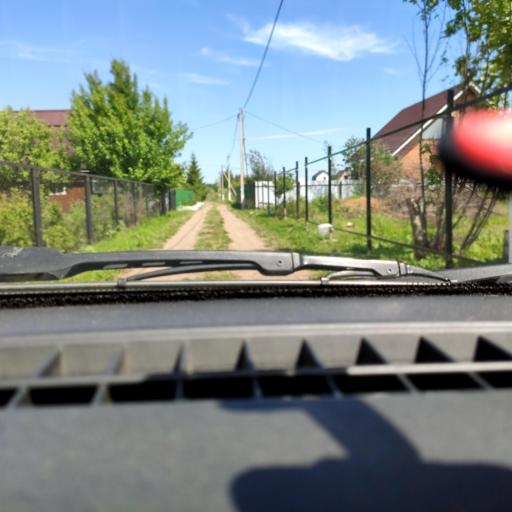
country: RU
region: Bashkortostan
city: Kabakovo
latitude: 54.7254
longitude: 56.2064
